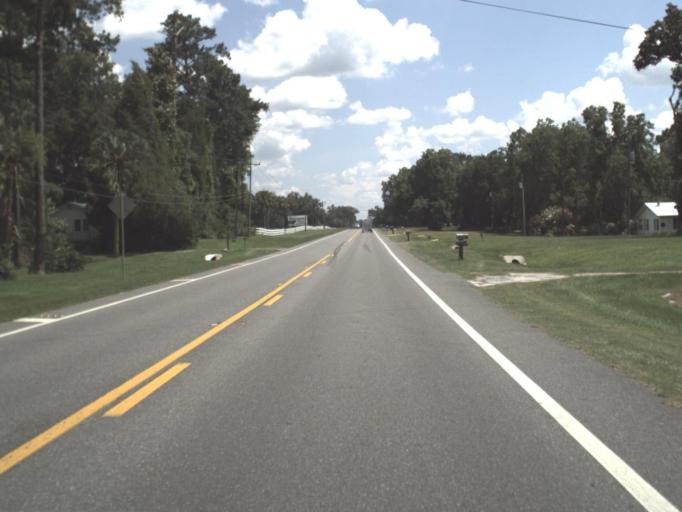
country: US
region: Florida
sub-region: Columbia County
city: Watertown
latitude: 30.0870
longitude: -82.6017
